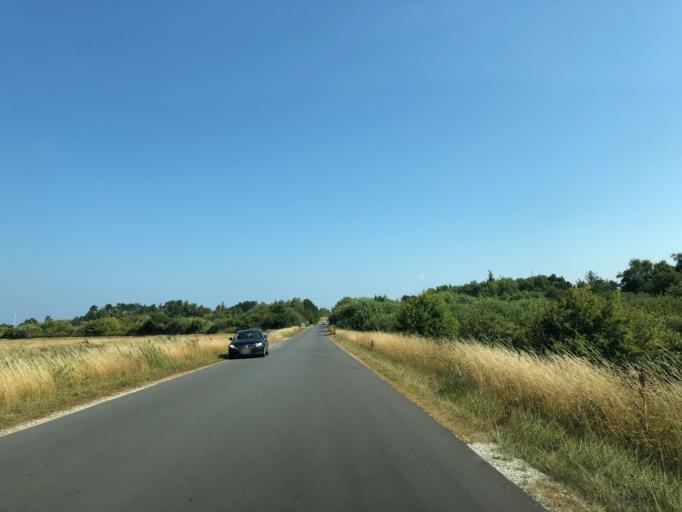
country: DK
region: Capital Region
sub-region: Halsnaes Kommune
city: Hundested
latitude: 55.9815
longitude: 11.8869
